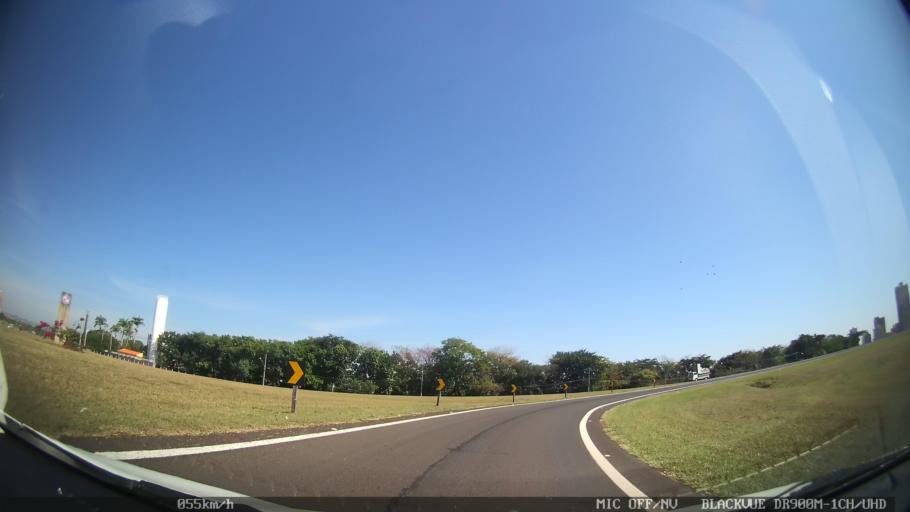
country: BR
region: Sao Paulo
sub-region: Ribeirao Preto
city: Ribeirao Preto
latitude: -21.2237
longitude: -47.8175
